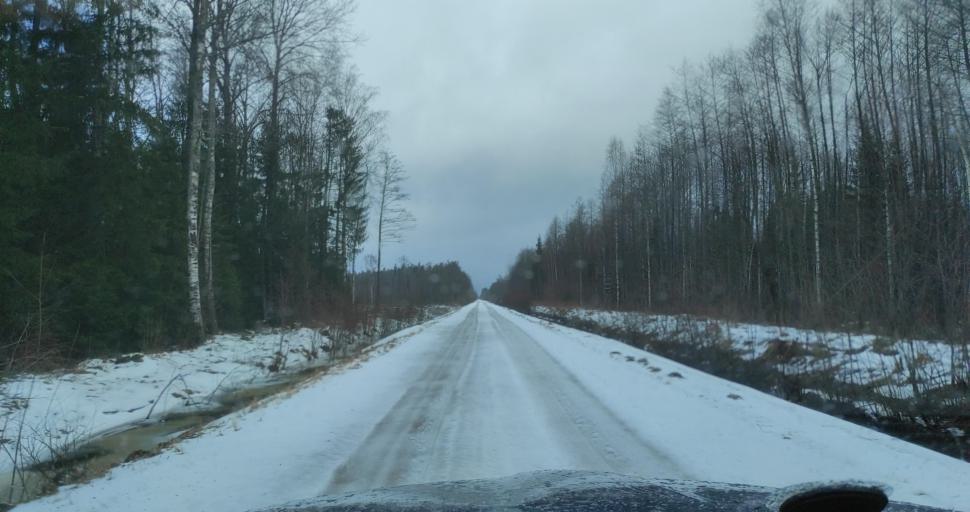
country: LV
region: Dundaga
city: Dundaga
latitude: 57.3945
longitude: 22.1224
